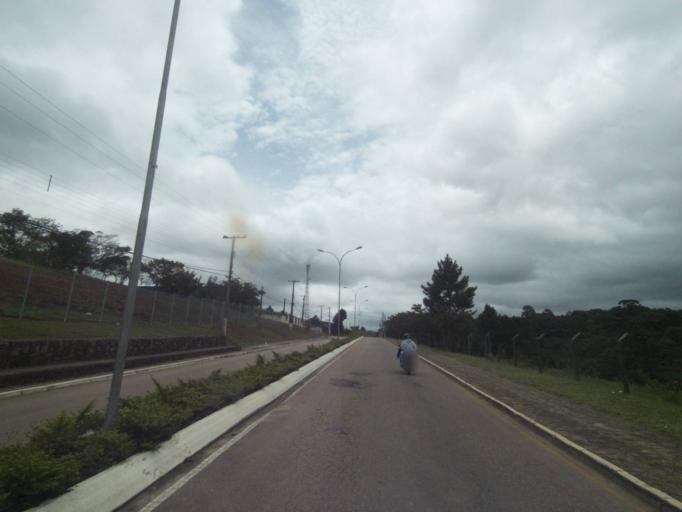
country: BR
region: Parana
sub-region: Campina Grande Do Sul
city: Campina Grande do Sul
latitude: -25.3076
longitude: -49.0597
